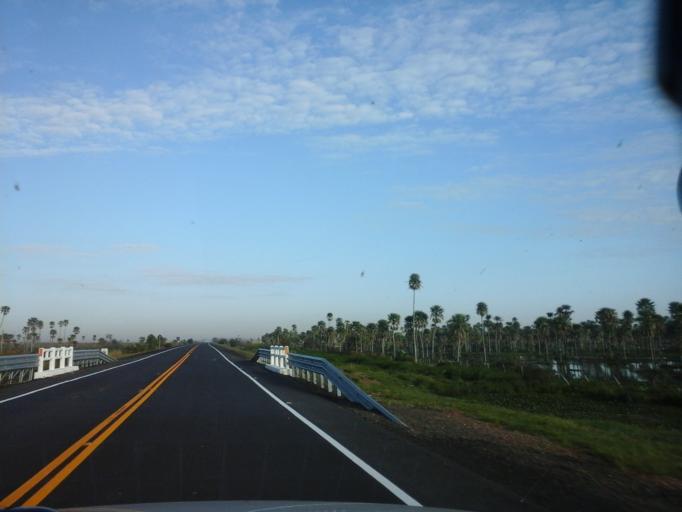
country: PY
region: Neembucu
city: Cerrito
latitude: -26.8680
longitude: -57.7652
